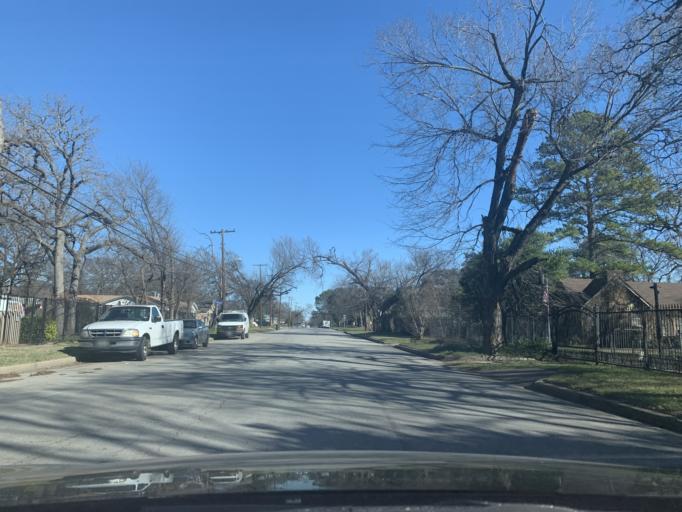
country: US
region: Texas
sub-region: Tarrant County
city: Haltom City
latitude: 32.7818
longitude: -97.2840
